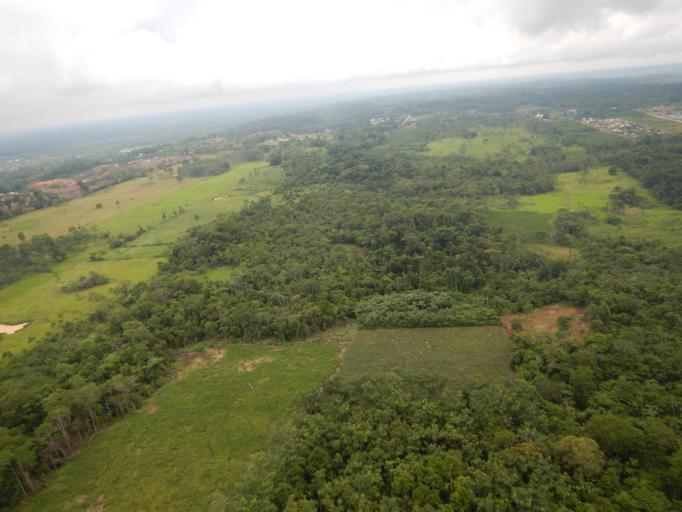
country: BO
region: Cochabamba
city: Chimore
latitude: -17.0772
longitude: -64.8575
